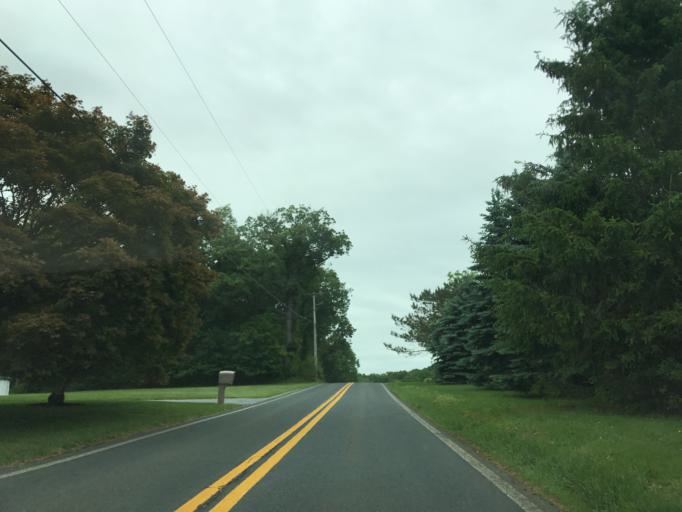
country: US
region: Maryland
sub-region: Carroll County
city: Hampstead
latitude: 39.5984
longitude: -76.8732
